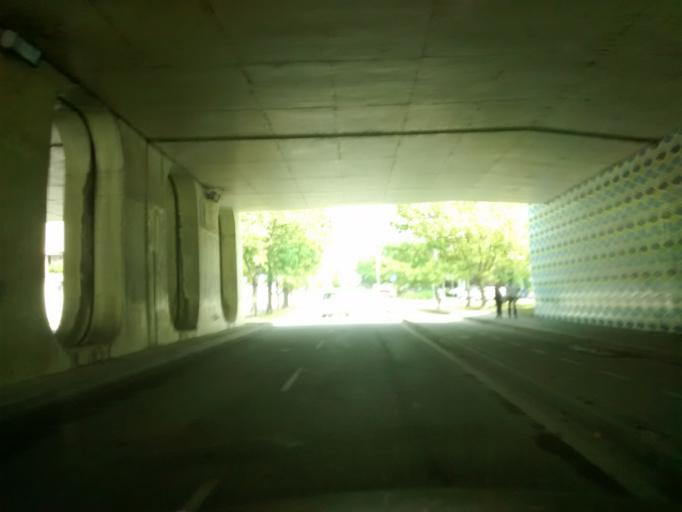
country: PT
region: Aveiro
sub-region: Aveiro
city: Aveiro
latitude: 40.6408
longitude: -8.6418
